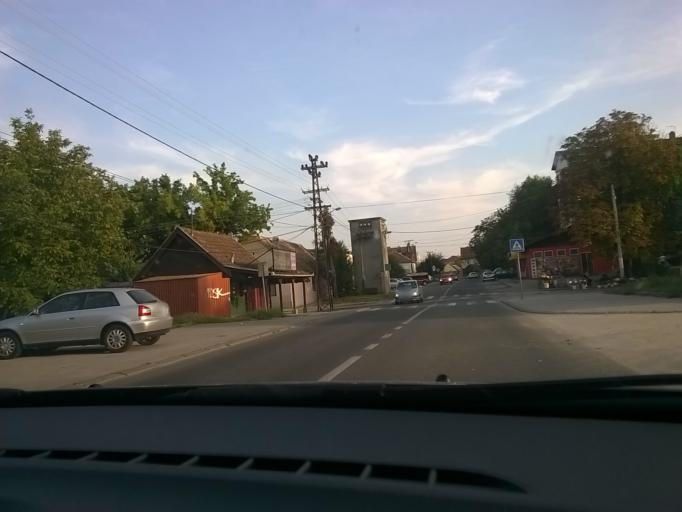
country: RS
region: Autonomna Pokrajina Vojvodina
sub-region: Juznobanatski Okrug
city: Vrsac
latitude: 45.1171
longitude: 21.2851
